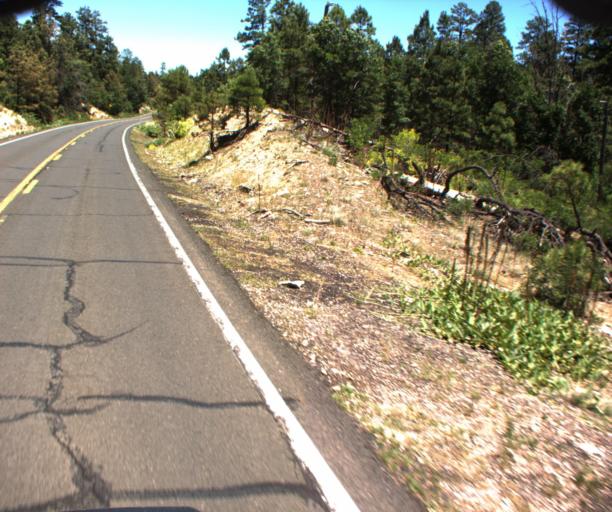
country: US
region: Arizona
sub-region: Gila County
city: Pine
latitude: 34.6035
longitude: -111.2373
